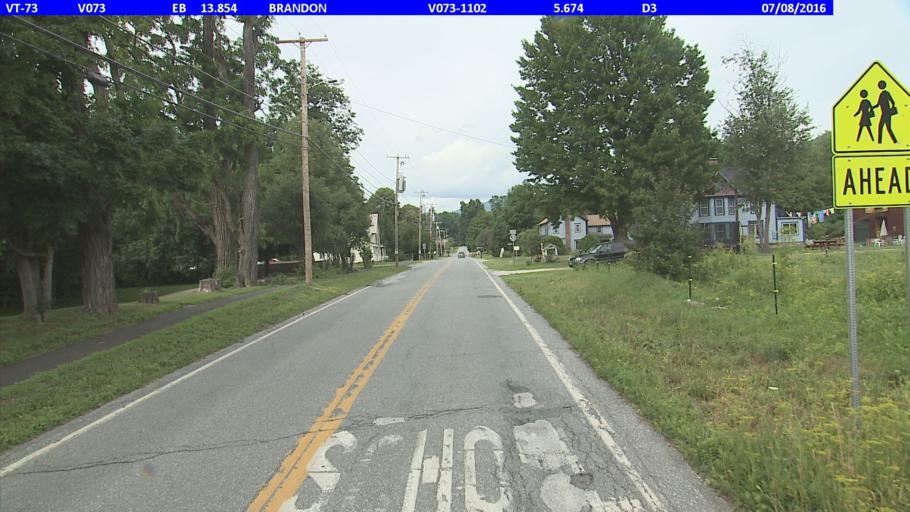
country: US
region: Vermont
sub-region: Rutland County
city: Brandon
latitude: 43.8247
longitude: -73.0556
